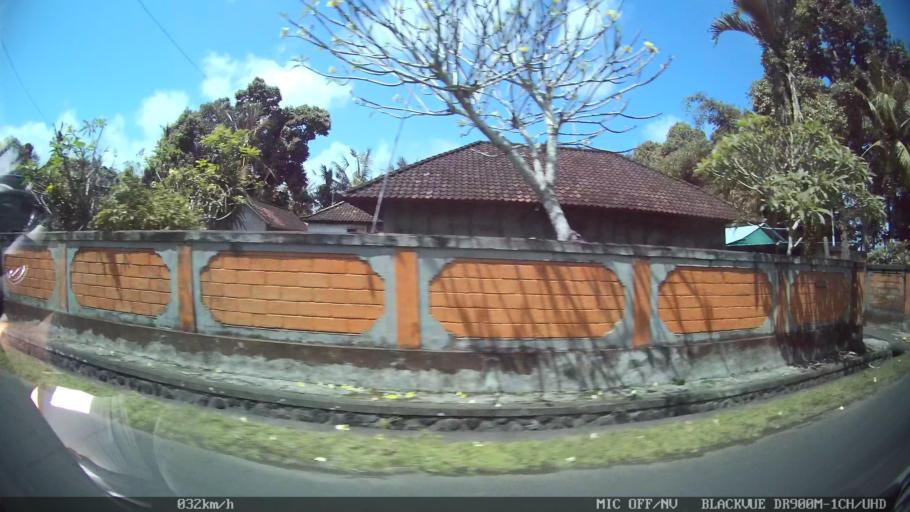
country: ID
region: Bali
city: Banjar Kelodan
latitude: -8.5257
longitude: 115.3340
